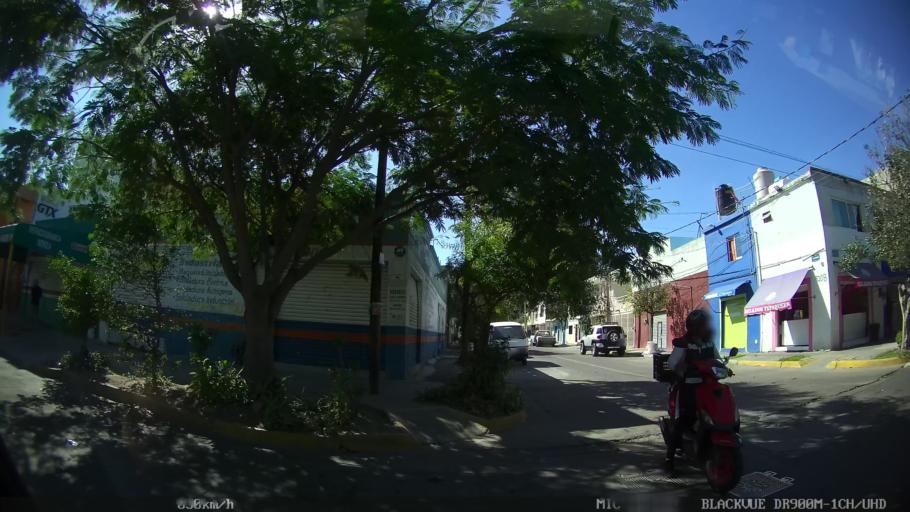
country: MX
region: Jalisco
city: Tlaquepaque
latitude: 20.6686
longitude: -103.2830
